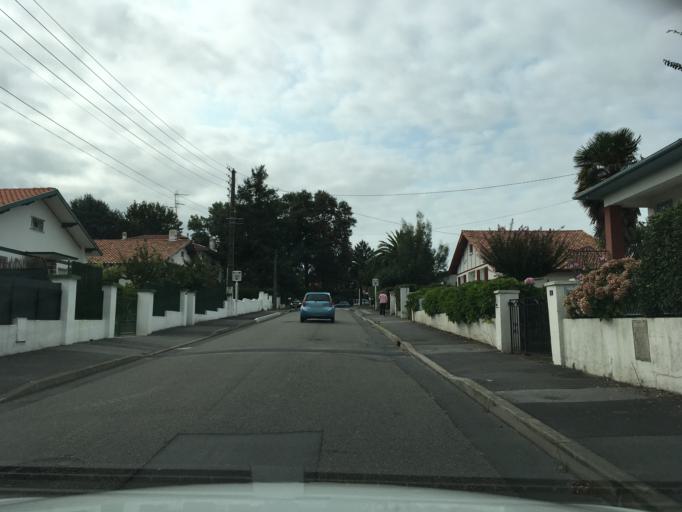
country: FR
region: Aquitaine
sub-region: Departement des Pyrenees-Atlantiques
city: Anglet
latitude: 43.4997
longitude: -1.5069
